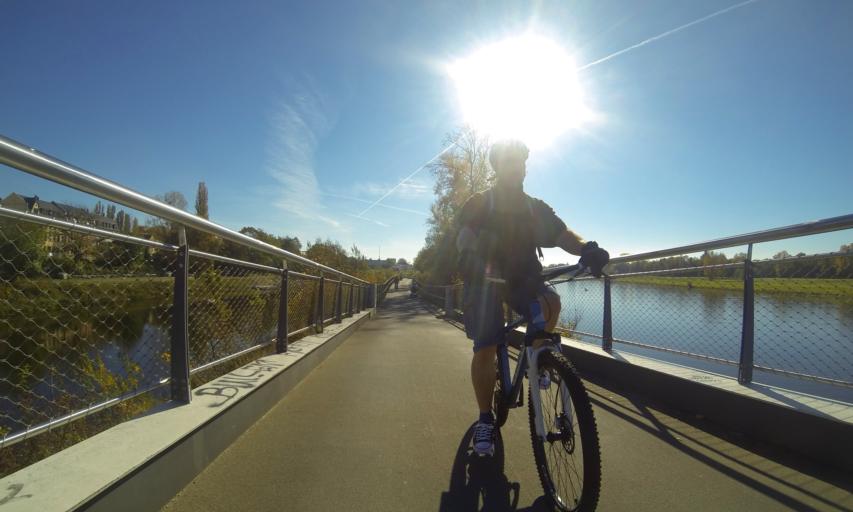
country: DE
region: Saxony
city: Dresden
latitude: 51.0759
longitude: 13.7189
